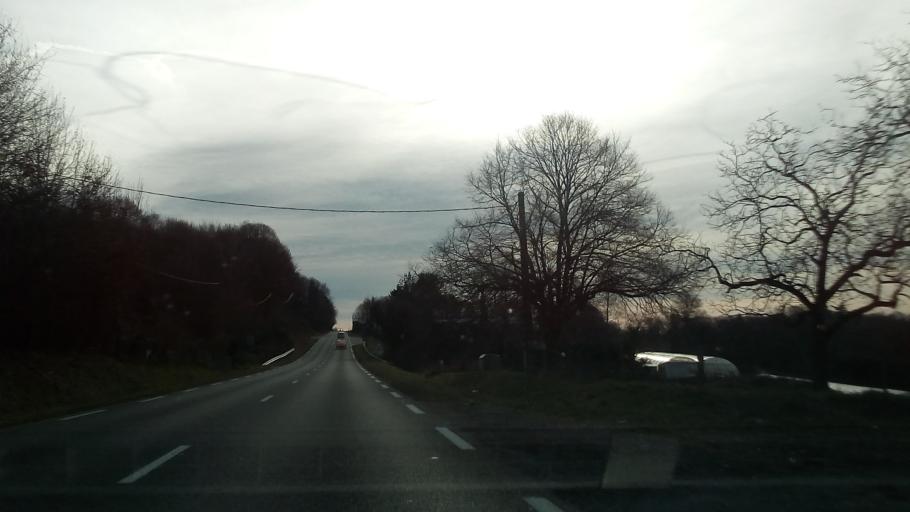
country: FR
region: Limousin
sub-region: Departement de la Correze
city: Seilhac
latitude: 45.3519
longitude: 1.7360
